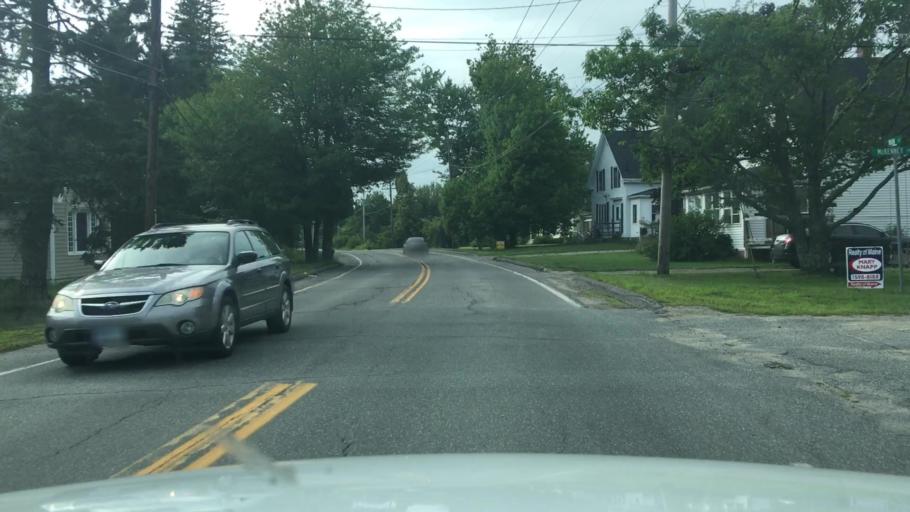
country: US
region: Maine
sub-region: Washington County
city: Addison
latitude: 44.6211
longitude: -67.8158
